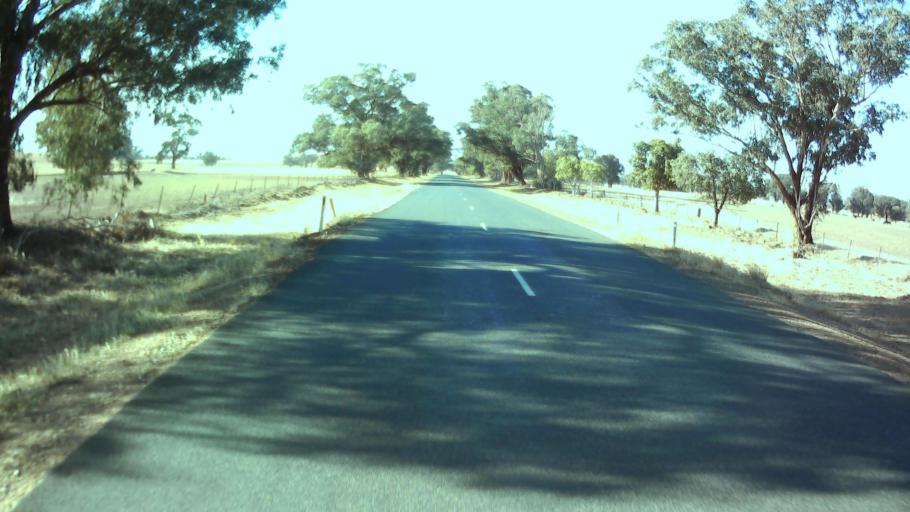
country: AU
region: New South Wales
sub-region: Weddin
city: Grenfell
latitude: -33.9597
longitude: 148.1399
